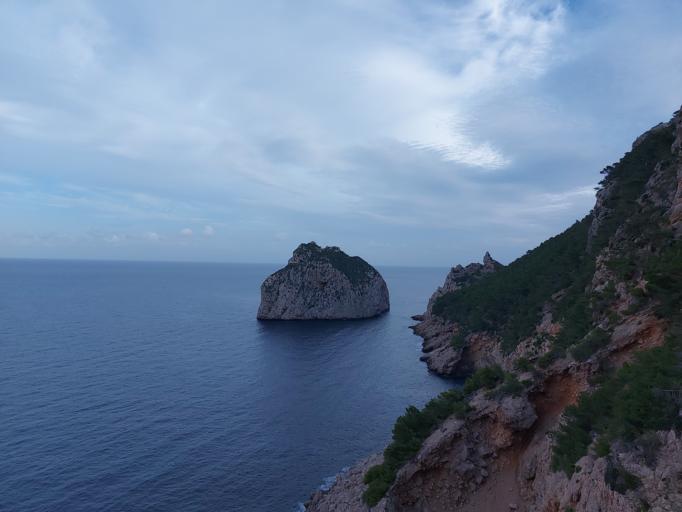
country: ES
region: Balearic Islands
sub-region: Illes Balears
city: Alcudia
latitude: 39.9380
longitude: 3.1313
